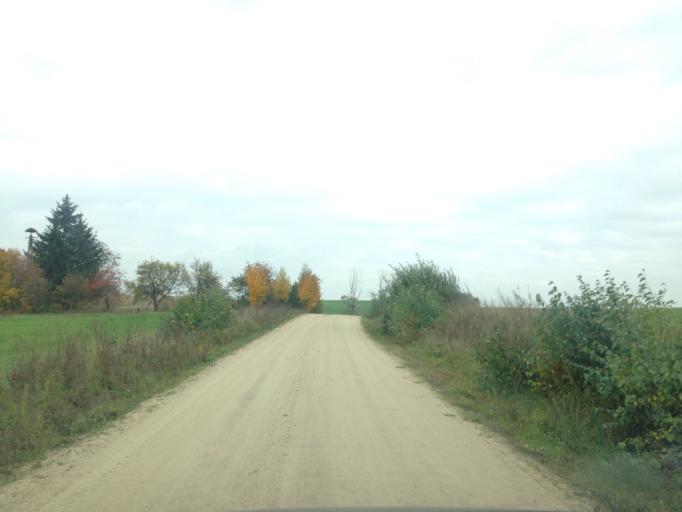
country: PL
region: Kujawsko-Pomorskie
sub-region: Powiat brodnicki
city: Brzozie
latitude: 53.3088
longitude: 19.6850
